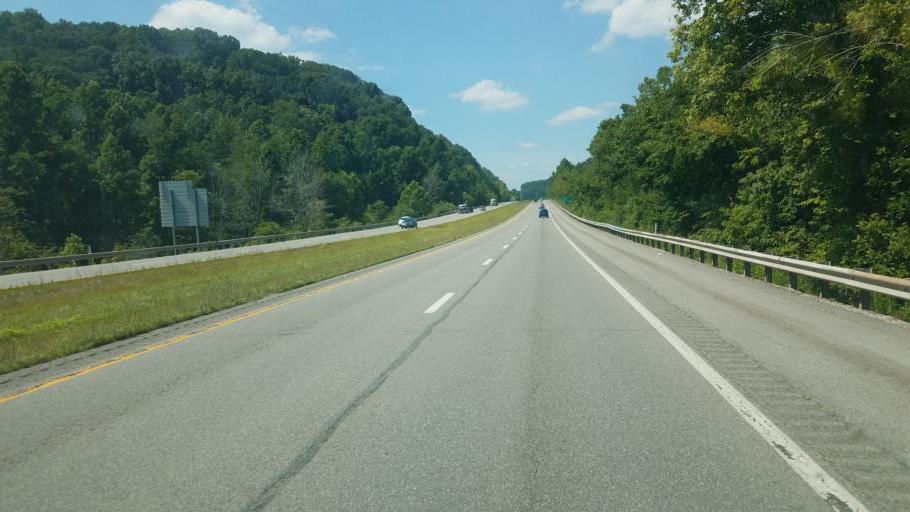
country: US
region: West Virginia
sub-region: Kanawha County
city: Sissonville
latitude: 38.6057
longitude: -81.6372
